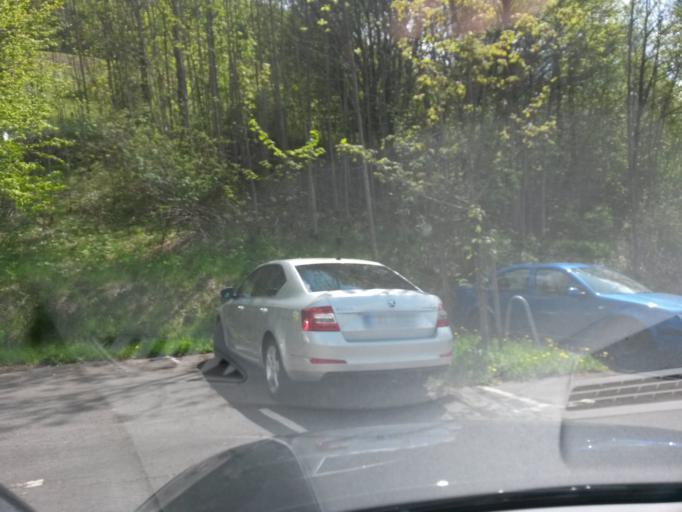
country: DE
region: Hesse
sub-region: Regierungsbezirk Kassel
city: Gersfeld
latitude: 50.4828
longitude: 9.9158
